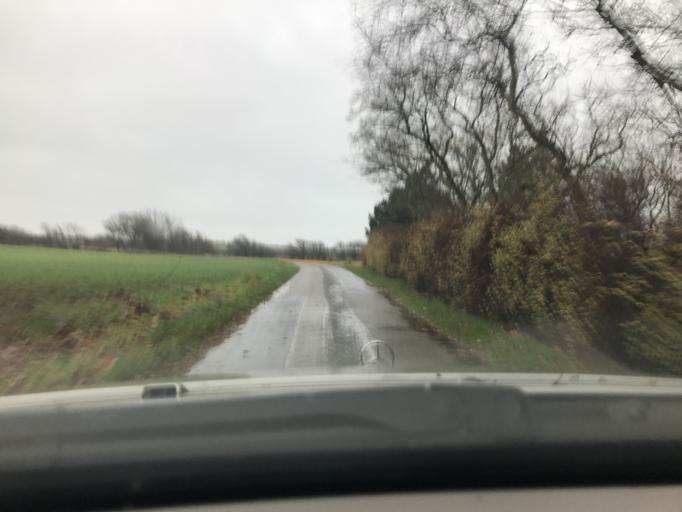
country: DK
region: South Denmark
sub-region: Sonderborg Kommune
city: Horuphav
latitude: 54.8750
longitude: 9.8777
